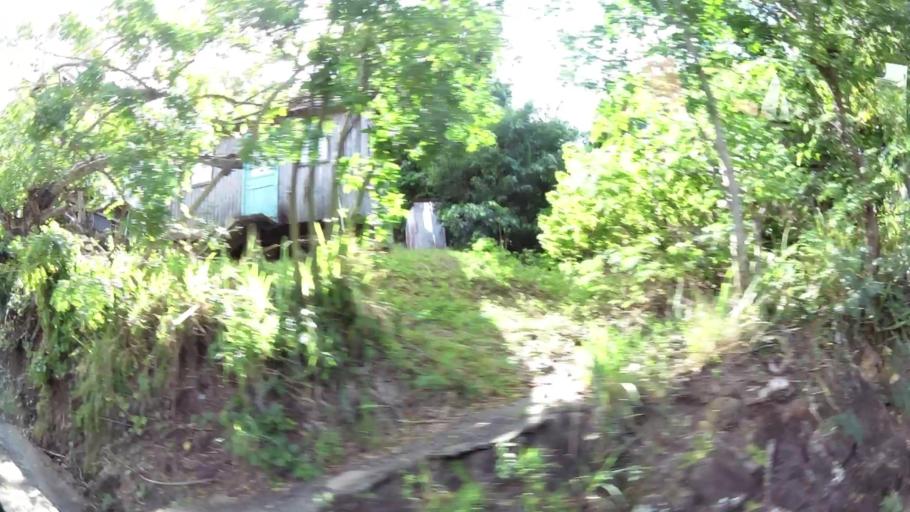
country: LC
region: Laborie Quarter
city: Laborie
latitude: 13.7508
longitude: -60.9940
